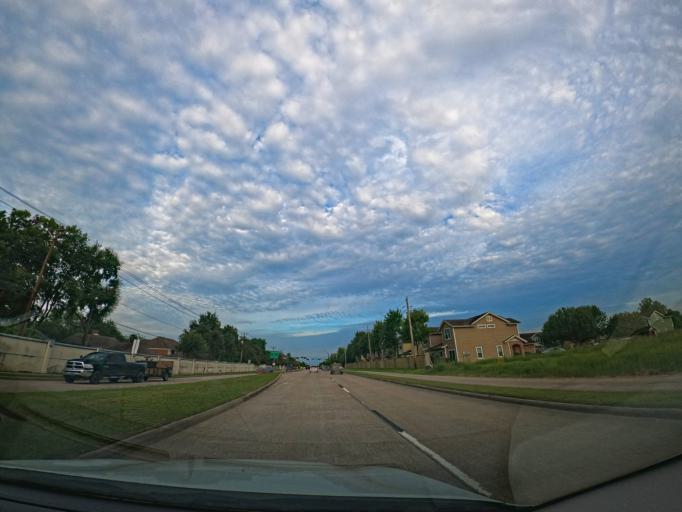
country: US
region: Texas
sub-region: Harris County
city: Nassau Bay
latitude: 29.5246
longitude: -95.0629
